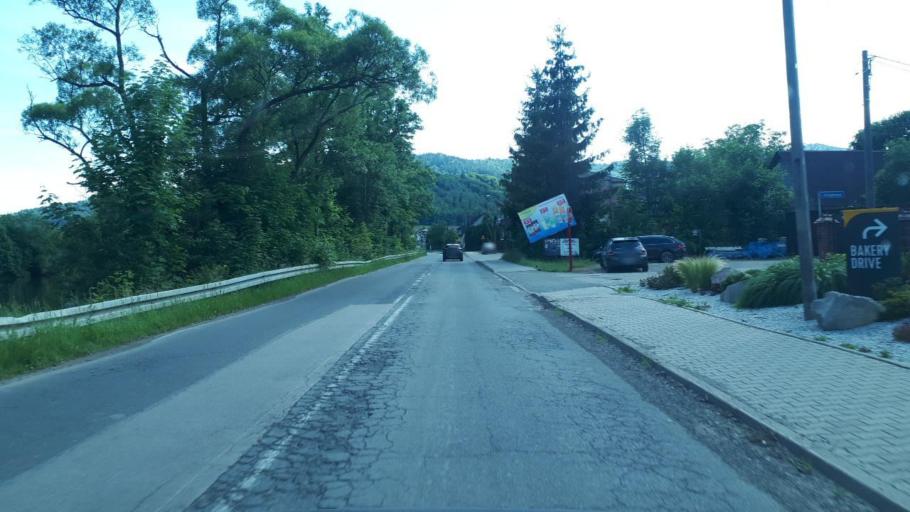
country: PL
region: Silesian Voivodeship
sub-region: Powiat zywiecki
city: Czernichow
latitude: 49.7555
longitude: 19.2118
